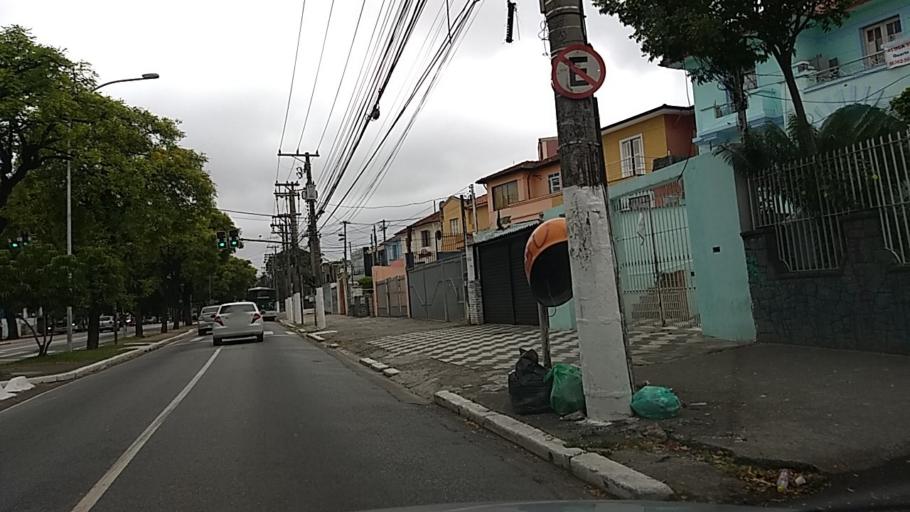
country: BR
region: Sao Paulo
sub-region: Sao Paulo
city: Sao Paulo
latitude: -23.5744
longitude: -46.6109
